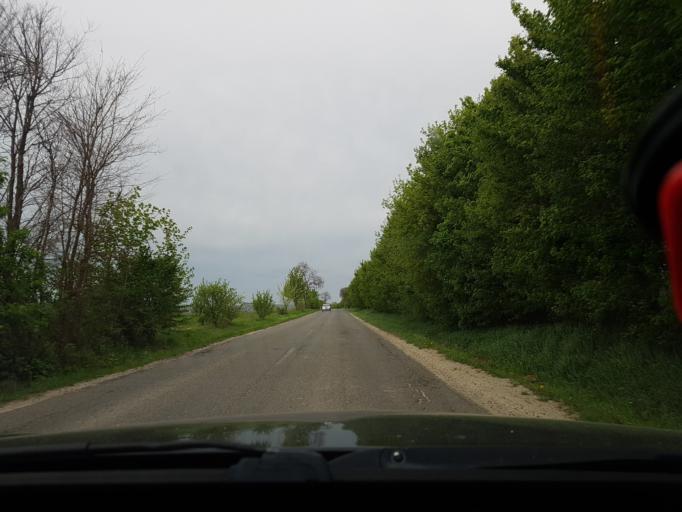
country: HU
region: Pest
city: Perbal
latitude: 47.5663
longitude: 18.7921
